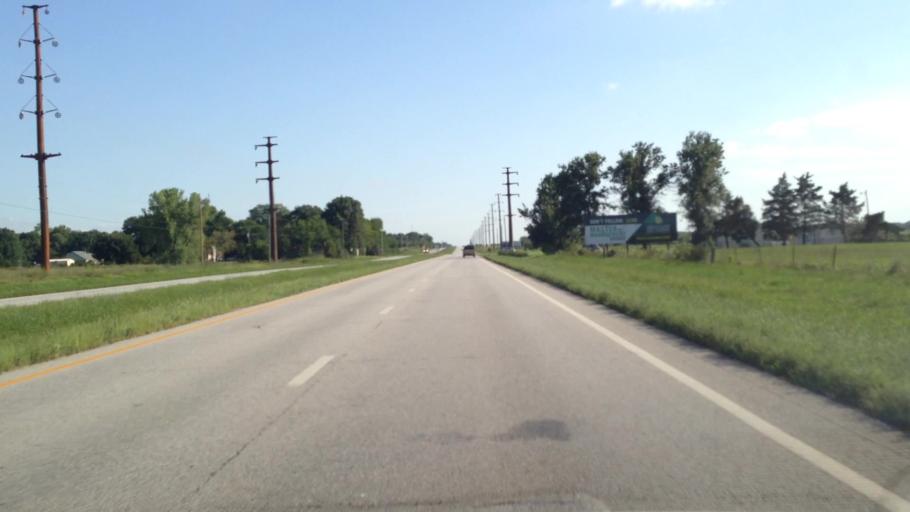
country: US
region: Kansas
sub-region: Crawford County
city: Arma
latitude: 37.5016
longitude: -94.7053
